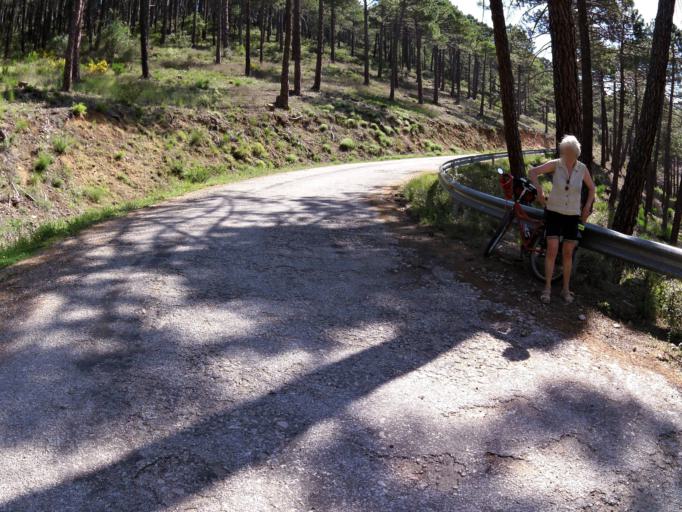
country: ES
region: Castille-La Mancha
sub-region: Provincia de Albacete
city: Riopar
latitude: 38.5238
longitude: -2.4375
